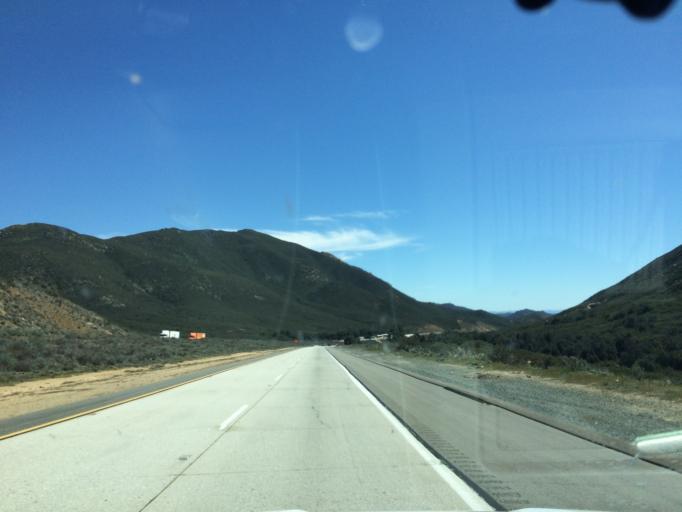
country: US
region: California
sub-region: San Diego County
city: Pine Valley
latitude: 32.8045
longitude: -116.5029
